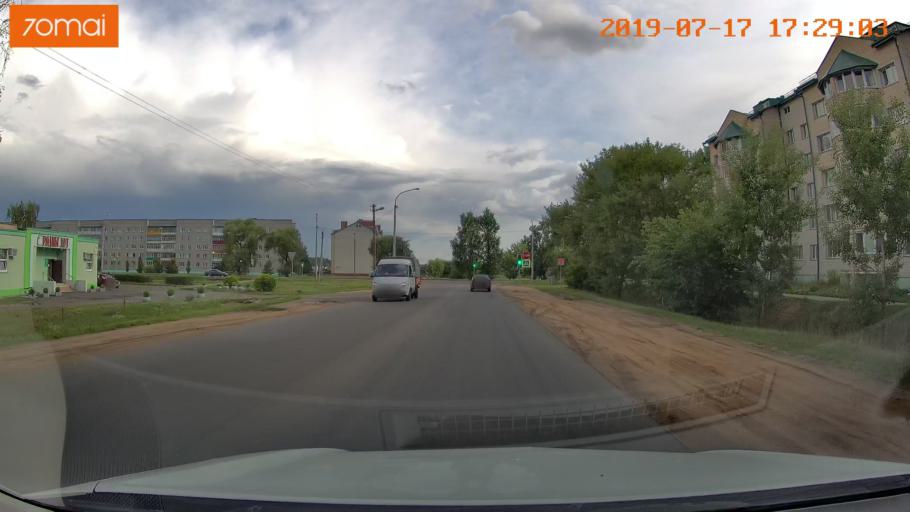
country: BY
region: Mogilev
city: Babruysk
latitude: 53.1241
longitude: 29.1664
